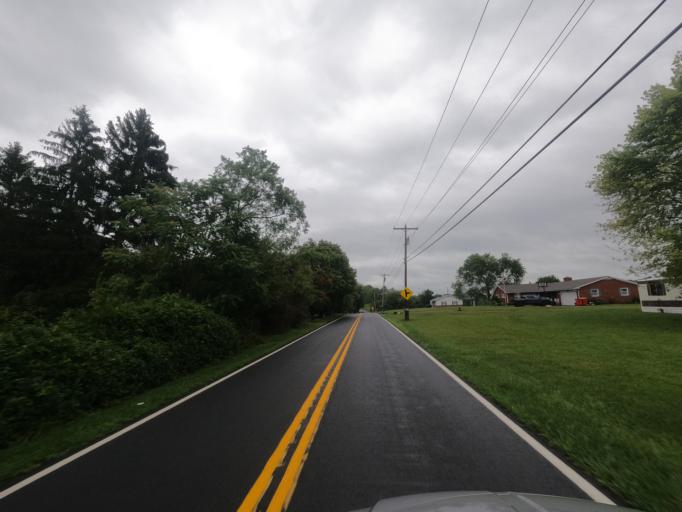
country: US
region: West Virginia
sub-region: Berkeley County
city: Martinsburg
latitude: 39.6181
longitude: -77.9955
